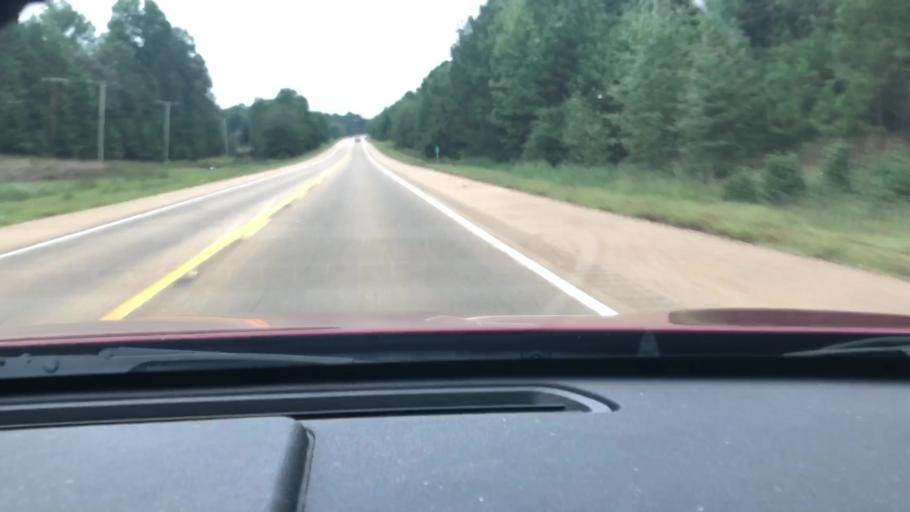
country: US
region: Arkansas
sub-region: Lafayette County
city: Stamps
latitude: 33.3589
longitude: -93.4218
